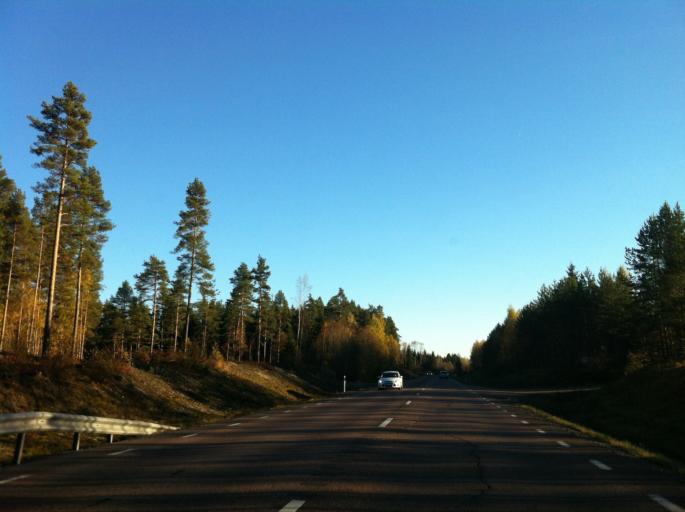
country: SE
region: Dalarna
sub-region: Faluns Kommun
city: Grycksbo
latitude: 60.6610
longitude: 15.5493
